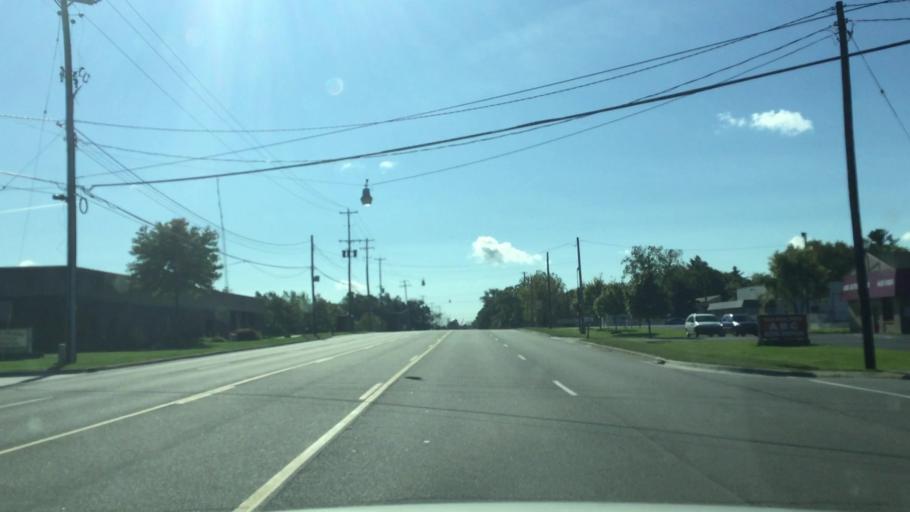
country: US
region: Michigan
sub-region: Genesee County
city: Grand Blanc
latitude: 42.9526
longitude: -83.6593
